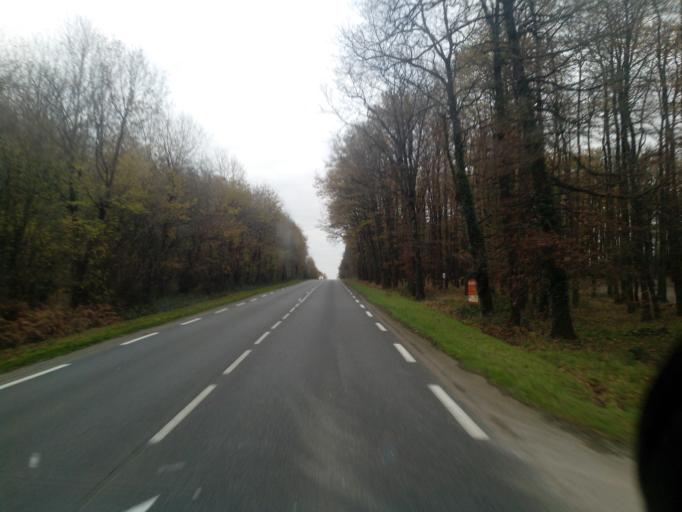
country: FR
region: Poitou-Charentes
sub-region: Departement des Deux-Sevres
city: Chiche
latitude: 46.8117
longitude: -0.3907
